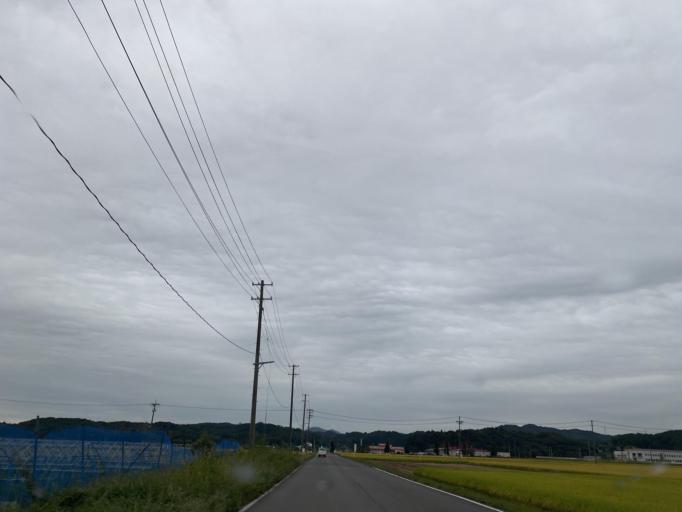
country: JP
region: Fukushima
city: Sukagawa
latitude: 37.2900
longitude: 140.2445
